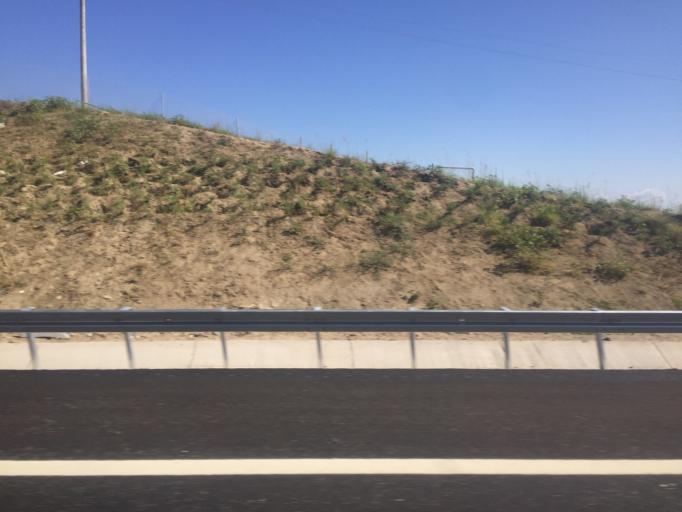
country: TR
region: Bursa
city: Gorukle
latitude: 40.2542
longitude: 28.7412
